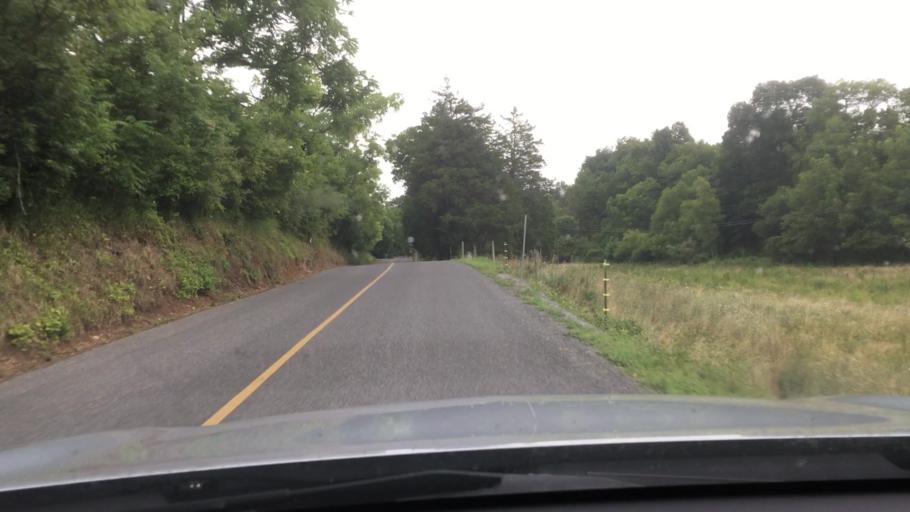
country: US
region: Pennsylvania
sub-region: Franklin County
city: Greencastle
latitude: 39.8763
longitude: -77.7888
